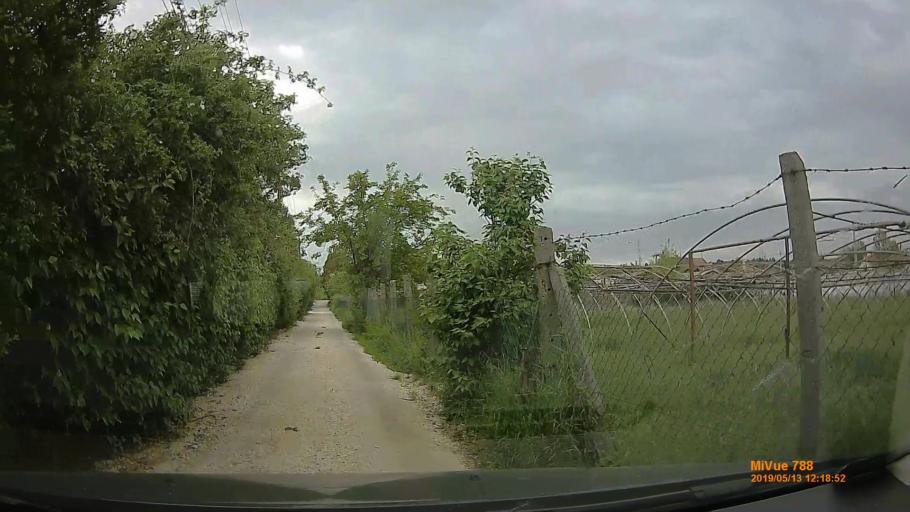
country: HU
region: Pest
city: Diosd
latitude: 47.4044
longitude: 18.9796
